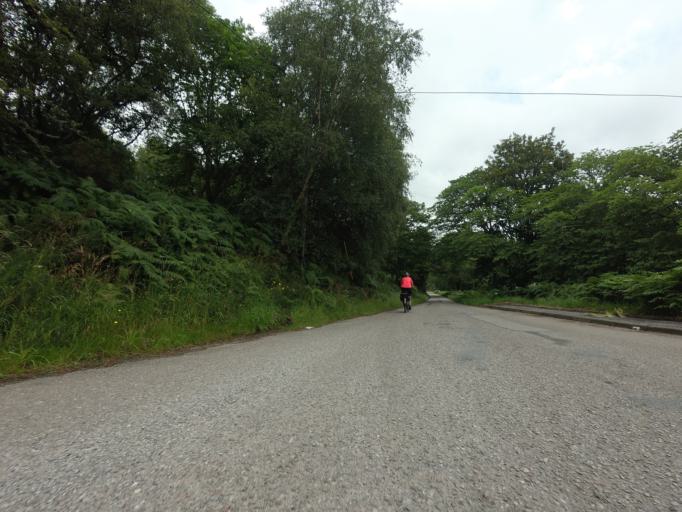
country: GB
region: Scotland
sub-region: Highland
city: Evanton
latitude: 57.9445
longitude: -4.4096
